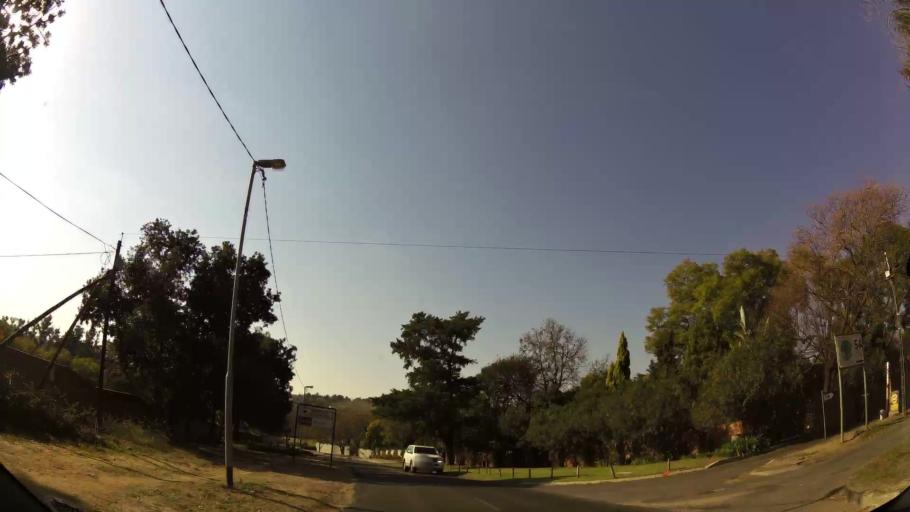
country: ZA
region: Gauteng
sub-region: City of Johannesburg Metropolitan Municipality
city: Diepsloot
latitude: -26.0626
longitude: 28.0125
